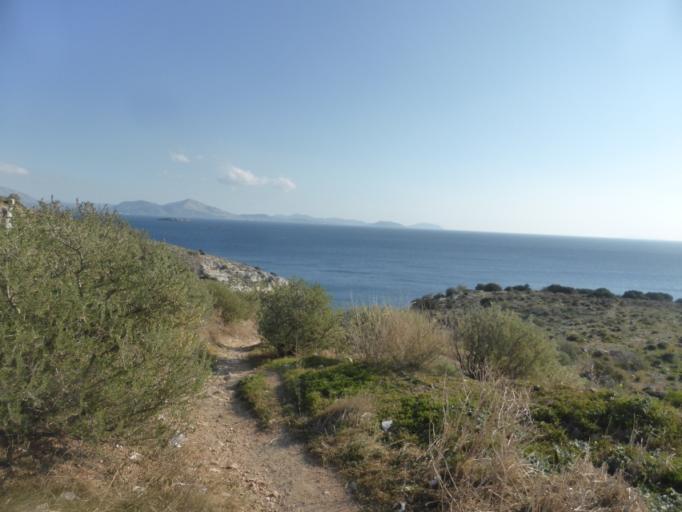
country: GR
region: Attica
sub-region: Nomarchia Anatolikis Attikis
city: Vouliagmeni
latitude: 37.8017
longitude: 23.7901
